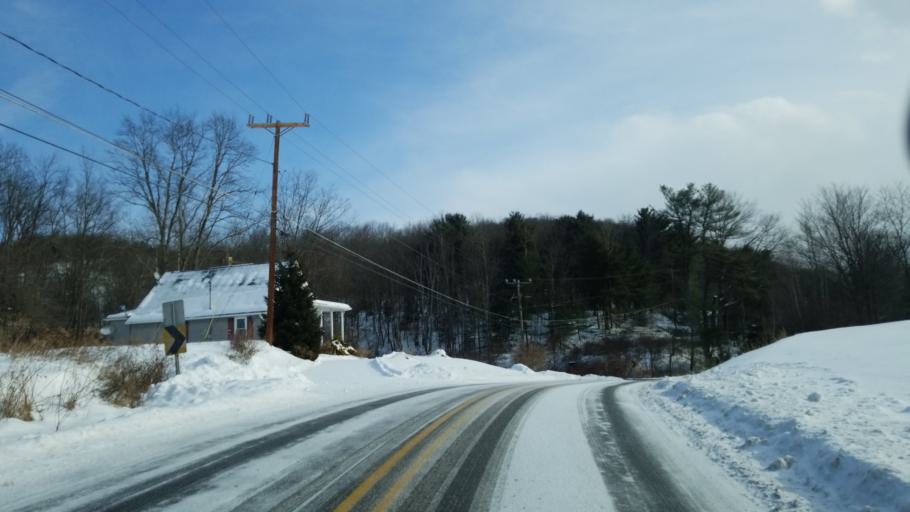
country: US
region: Pennsylvania
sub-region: Clearfield County
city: Hyde
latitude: 41.0163
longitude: -78.4592
